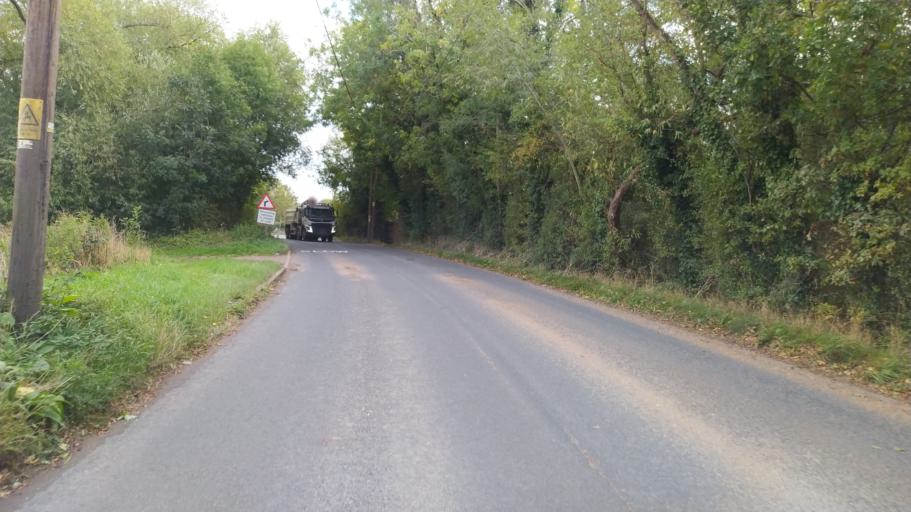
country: GB
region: England
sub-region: Wokingham
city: Shinfield
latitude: 51.4122
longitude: -0.9811
